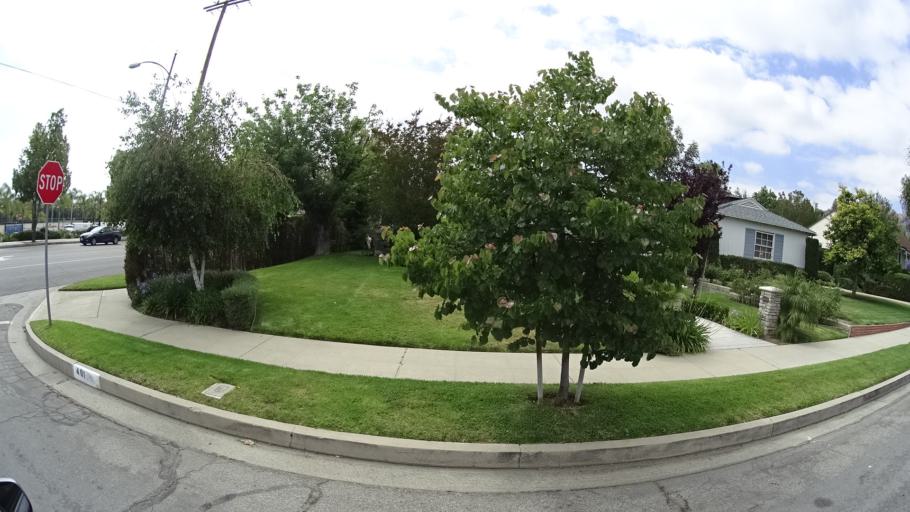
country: US
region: California
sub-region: Los Angeles County
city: Burbank
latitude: 34.1931
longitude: -118.3192
